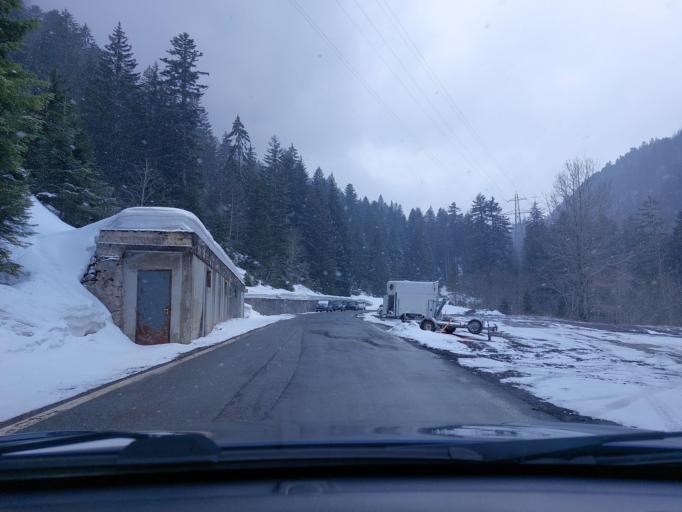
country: CH
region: Valais
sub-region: Sion District
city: Saviese
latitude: 46.2990
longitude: 7.3212
